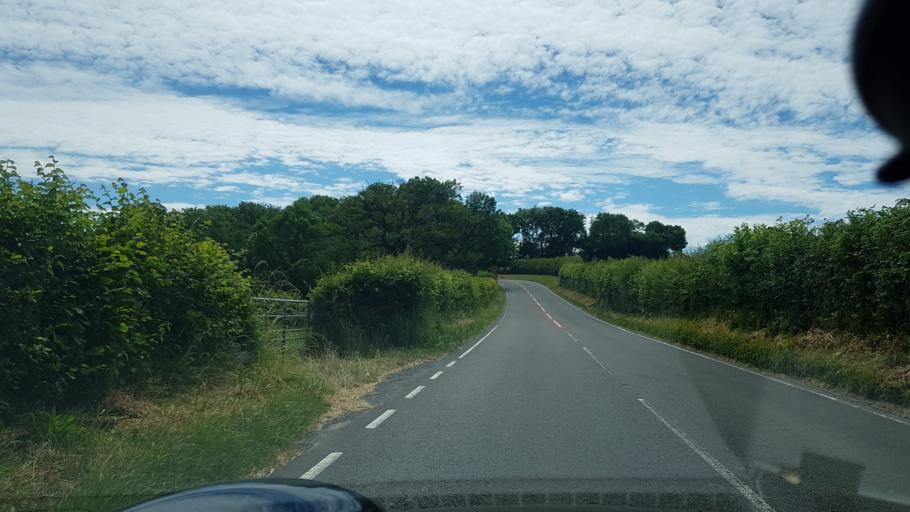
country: GB
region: Wales
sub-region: Carmarthenshire
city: Saint Clears
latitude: 51.8057
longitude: -4.4967
